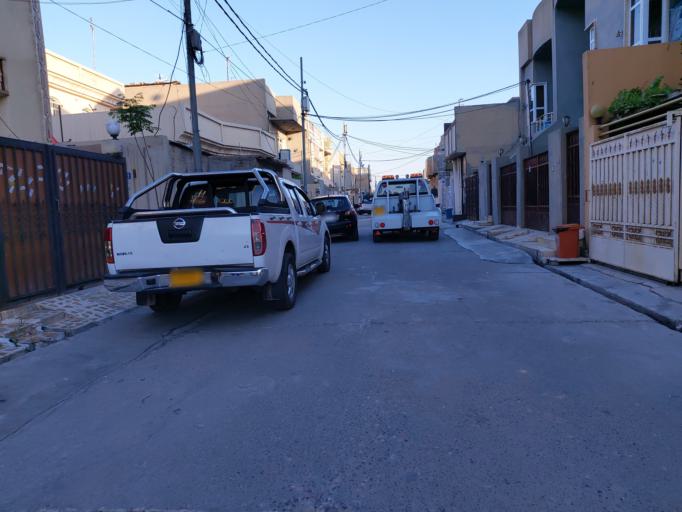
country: IQ
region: Arbil
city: Erbil
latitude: 36.1592
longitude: 43.9917
